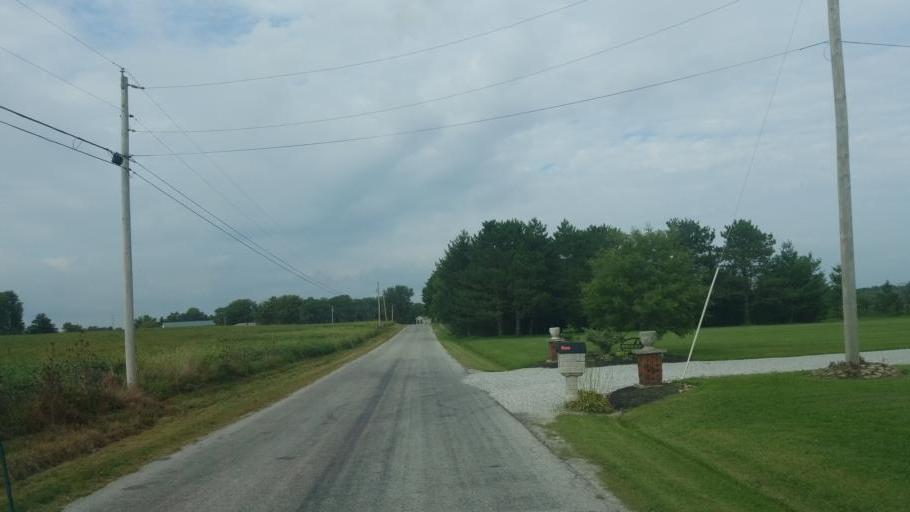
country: US
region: Ohio
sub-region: Wayne County
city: West Salem
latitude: 40.9496
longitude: -82.0548
